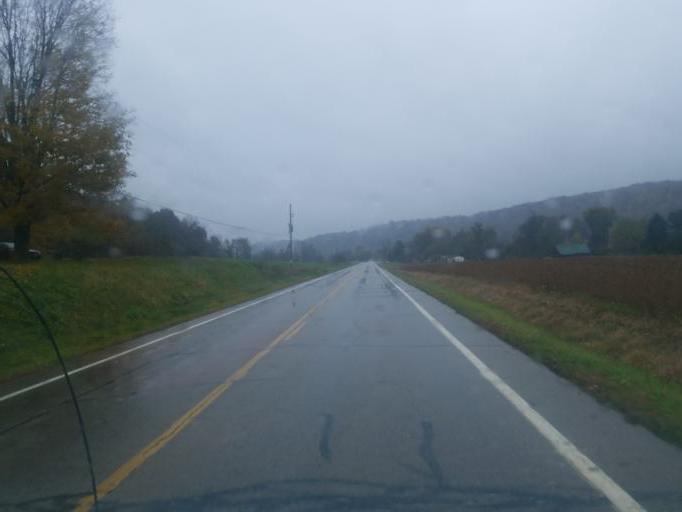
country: US
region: Ohio
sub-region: Morgan County
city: McConnelsville
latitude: 39.7436
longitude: -81.9132
